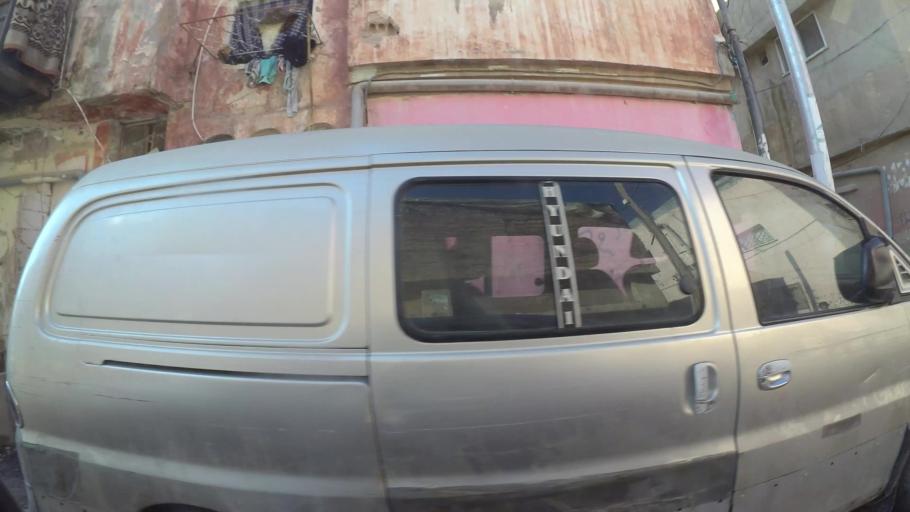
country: JO
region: Amman
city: Al Jubayhah
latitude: 32.0754
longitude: 35.8412
